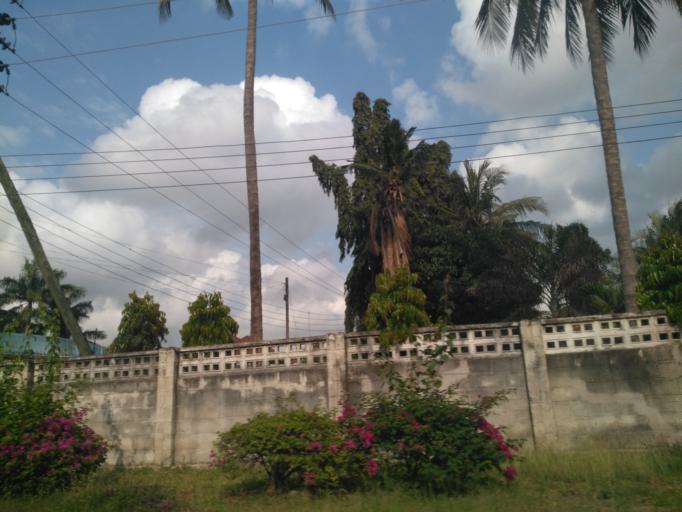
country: TZ
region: Dar es Salaam
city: Magomeni
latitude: -6.7479
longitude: 39.2358
